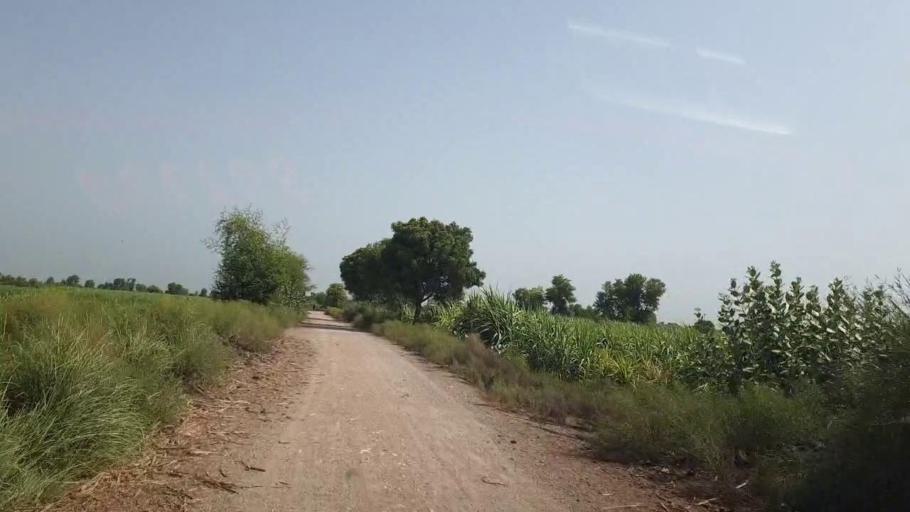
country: PK
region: Sindh
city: Sakrand
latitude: 26.3064
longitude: 68.2113
